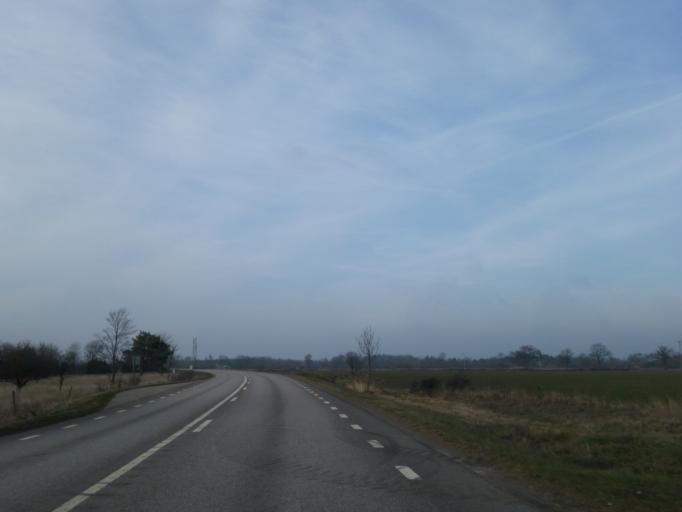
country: SE
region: Kalmar
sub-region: Borgholms Kommun
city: Borgholm
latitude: 56.8887
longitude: 16.7320
